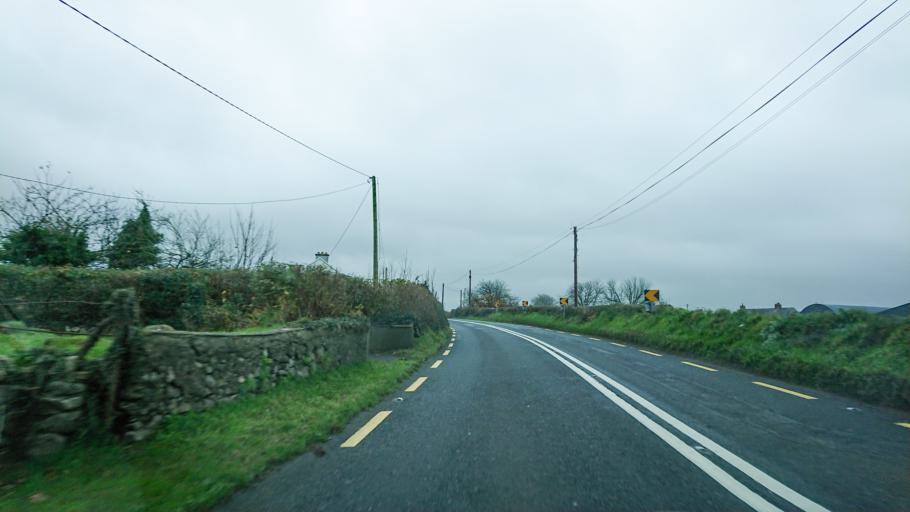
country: IE
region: Leinster
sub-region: Kilkenny
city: Mooncoin
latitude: 52.3036
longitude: -7.2762
